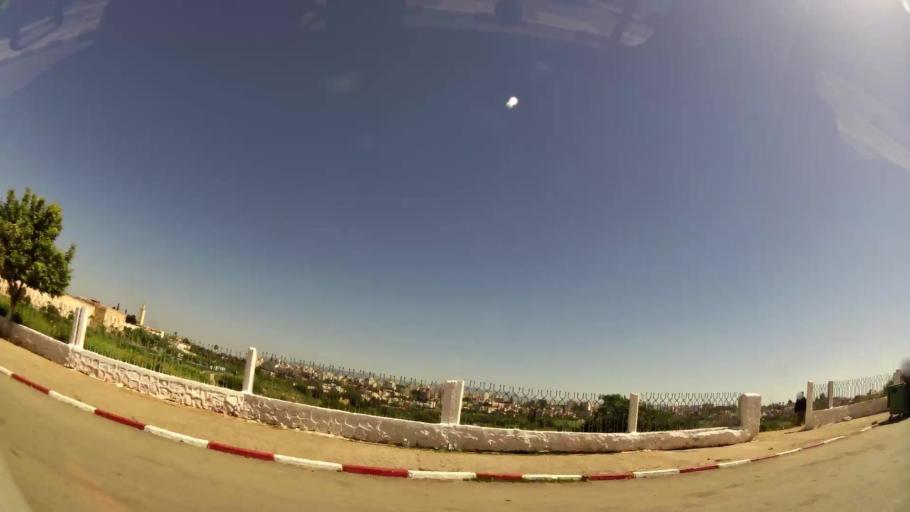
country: MA
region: Meknes-Tafilalet
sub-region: Meknes
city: Meknes
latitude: 33.8852
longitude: -5.5521
